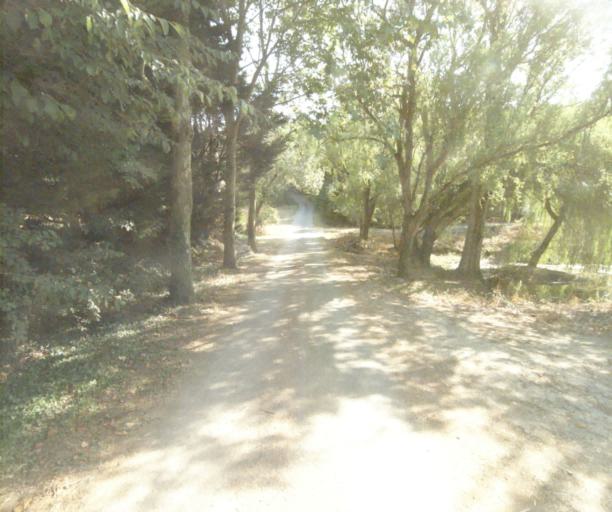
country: FR
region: Midi-Pyrenees
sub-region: Departement de la Haute-Garonne
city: Saint-Felix-Lauragais
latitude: 43.4304
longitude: 1.8284
